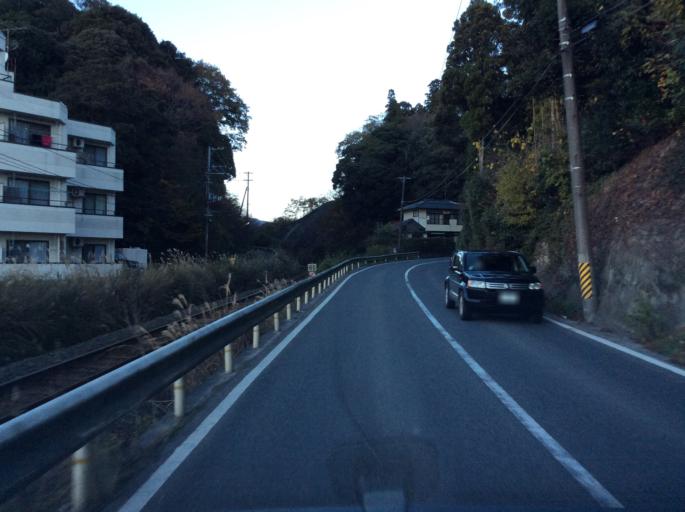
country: JP
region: Fukushima
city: Iwaki
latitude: 37.0888
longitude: 140.8617
